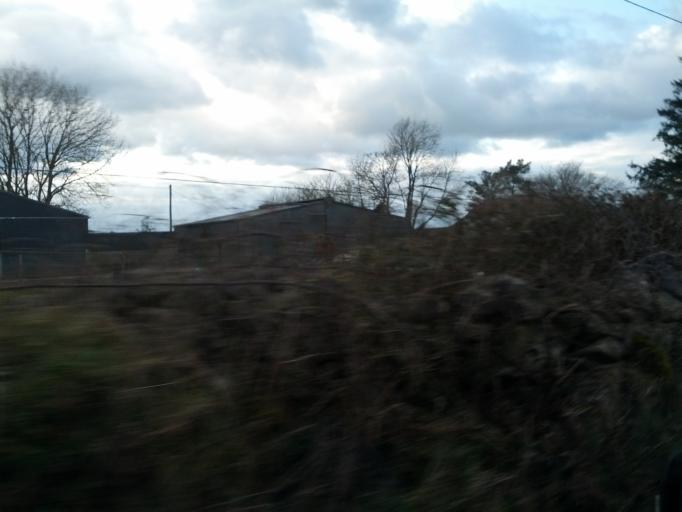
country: IE
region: Connaught
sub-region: County Galway
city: Tuam
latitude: 53.4286
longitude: -8.7595
